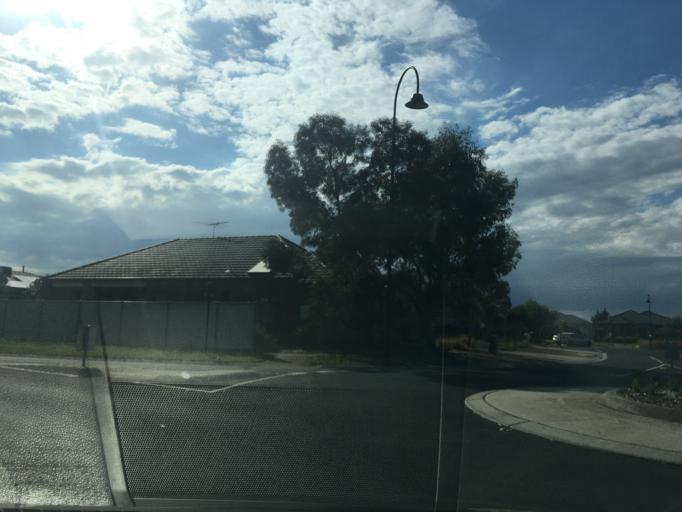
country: AU
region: Victoria
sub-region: Wyndham
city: Williams Landing
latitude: -37.8808
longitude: 144.7318
